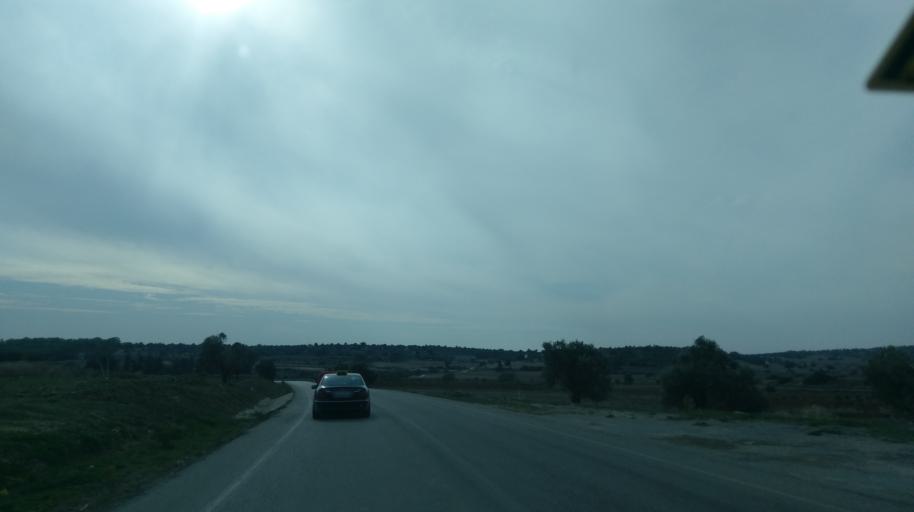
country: CY
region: Ammochostos
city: Leonarisso
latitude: 35.4567
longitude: 34.1292
